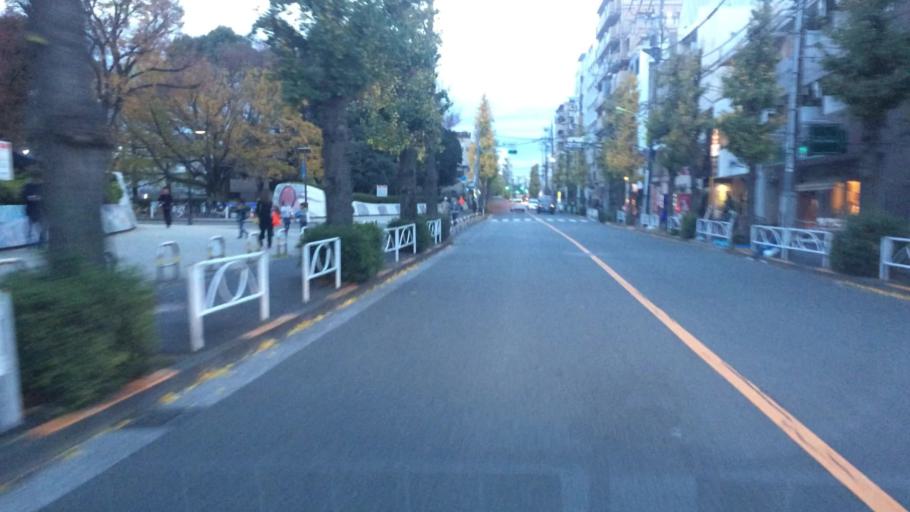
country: JP
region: Tokyo
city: Tokyo
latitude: 35.6286
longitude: 139.6563
